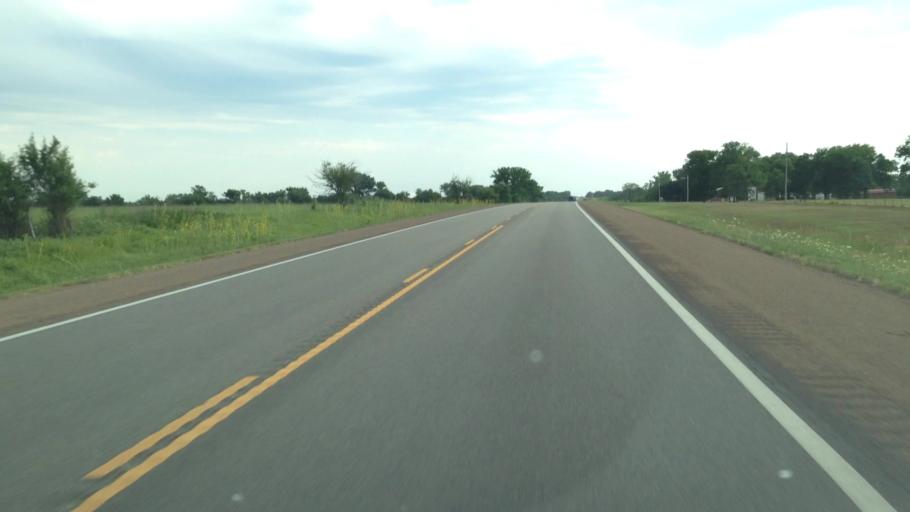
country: US
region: Kansas
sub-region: Woodson County
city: Yates Center
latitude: 38.0070
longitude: -95.7389
